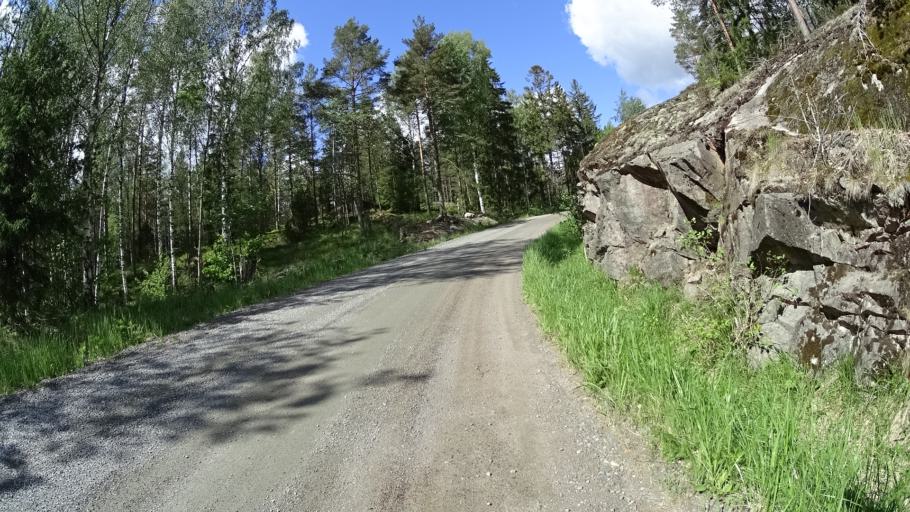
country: FI
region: Uusimaa
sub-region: Raaseporin
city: Pohja
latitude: 60.1748
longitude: 23.5852
